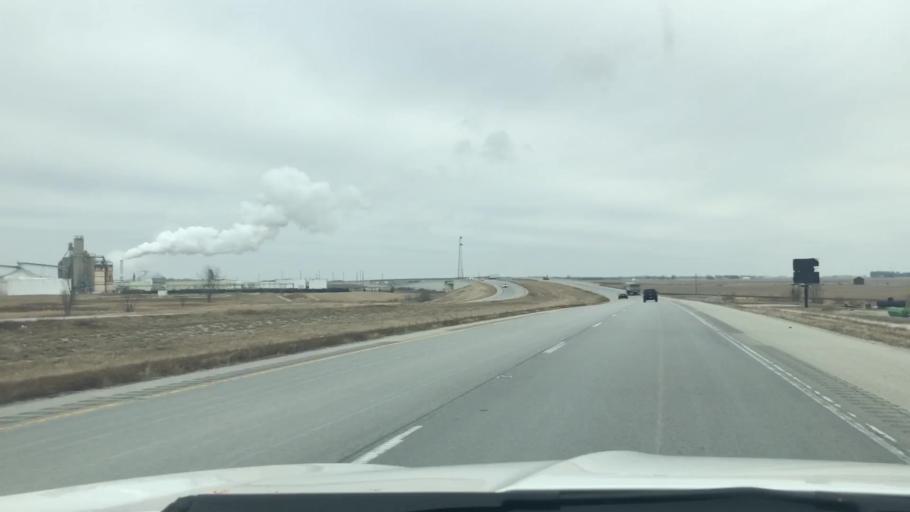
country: US
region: Indiana
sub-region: Cass County
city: Georgetown
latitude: 40.7106
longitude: -86.4464
